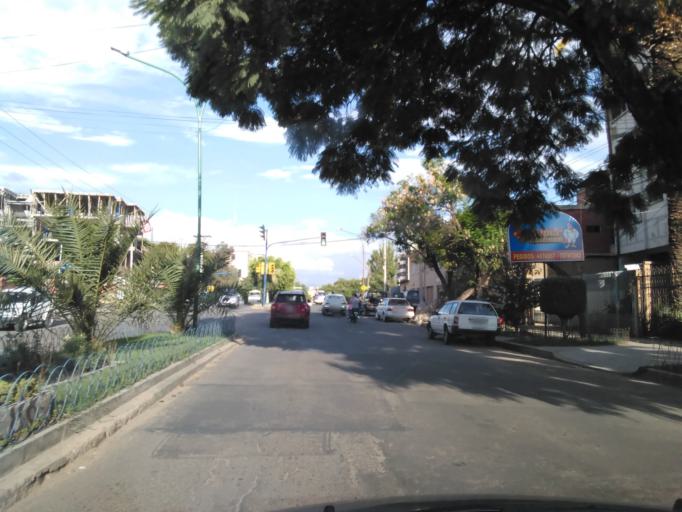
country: BO
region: Cochabamba
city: Cochabamba
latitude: -17.3658
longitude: -66.1723
